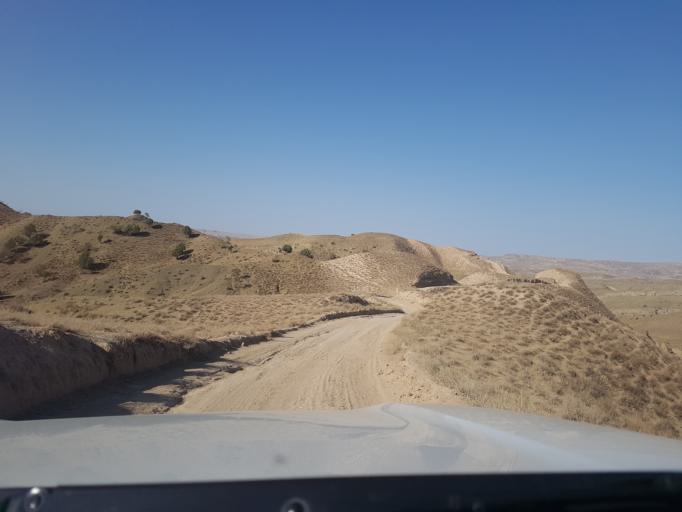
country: TM
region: Balkan
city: Magtymguly
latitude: 38.3035
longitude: 56.8011
